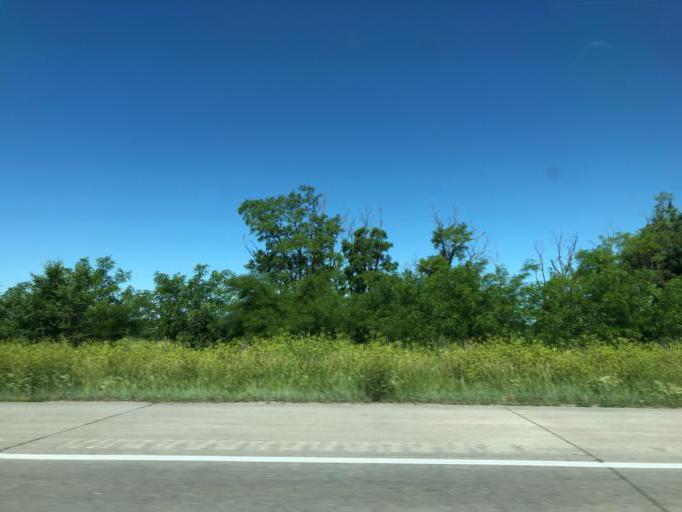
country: US
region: Nebraska
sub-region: Saunders County
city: Ashland
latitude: 41.0588
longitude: -96.2958
